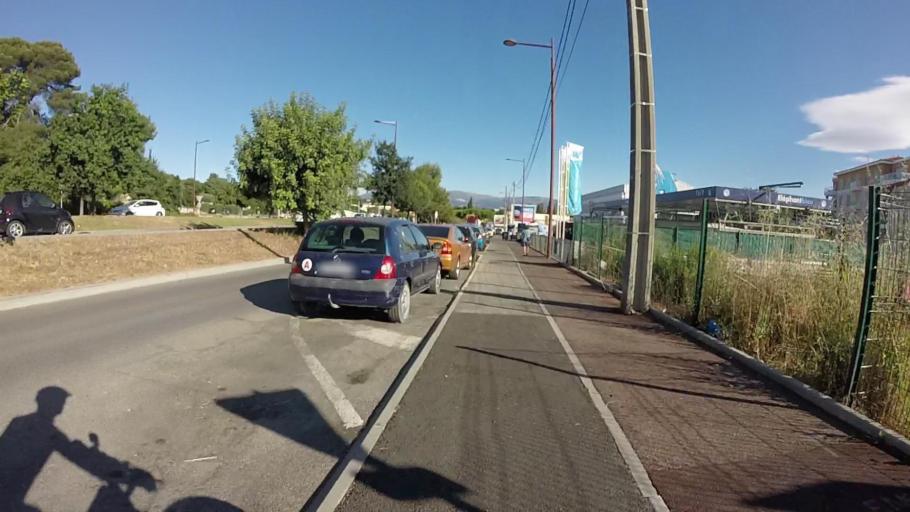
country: FR
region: Provence-Alpes-Cote d'Azur
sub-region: Departement des Alpes-Maritimes
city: Biot
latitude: 43.5969
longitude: 7.0900
